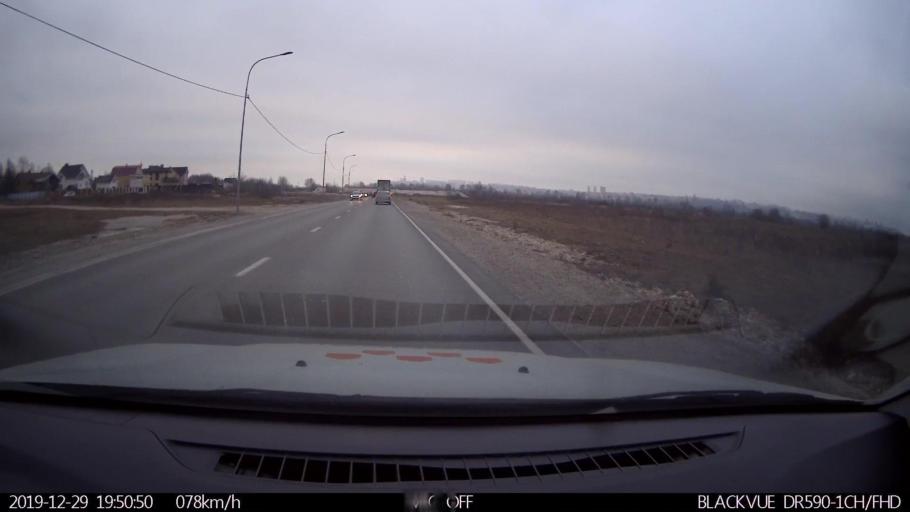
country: RU
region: Nizjnij Novgorod
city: Bor
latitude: 56.3638
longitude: 44.0323
